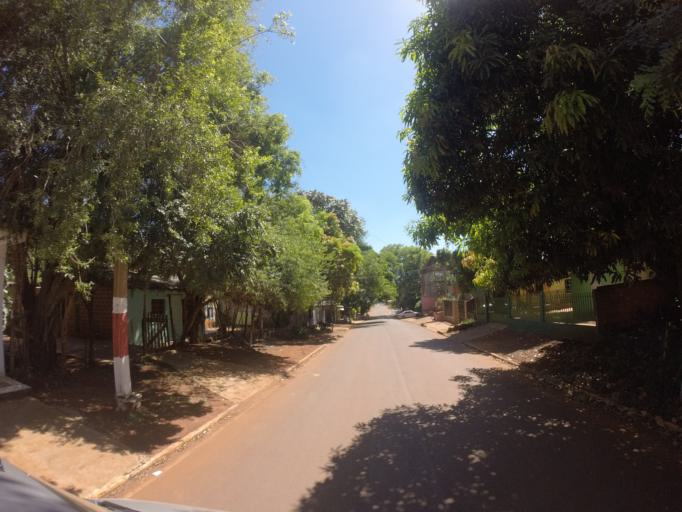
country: PY
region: Alto Parana
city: Ciudad del Este
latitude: -25.4348
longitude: -54.6439
